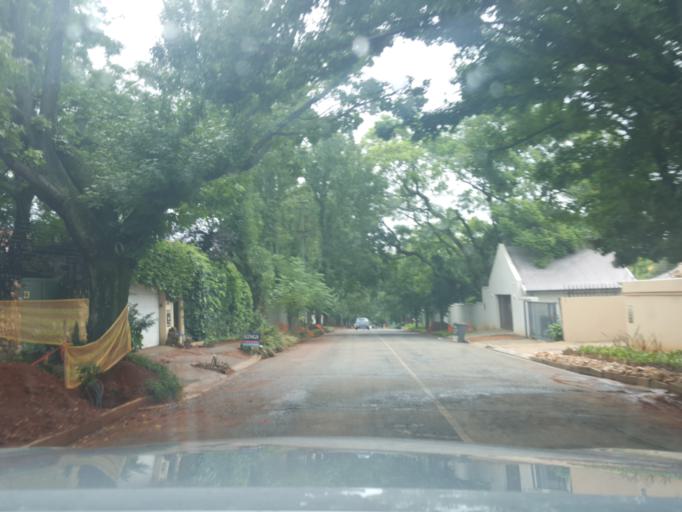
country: ZA
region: Gauteng
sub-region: City of Johannesburg Metropolitan Municipality
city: Johannesburg
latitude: -26.1493
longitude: 28.0149
